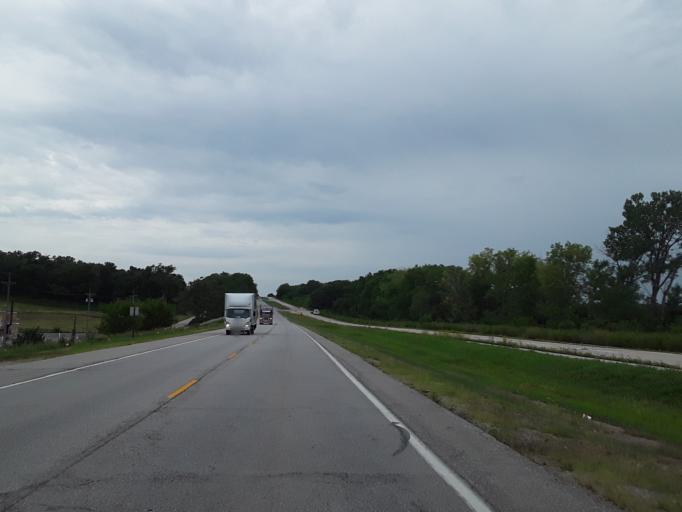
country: US
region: Nebraska
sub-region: Douglas County
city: Bennington
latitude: 41.3650
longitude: -96.0566
